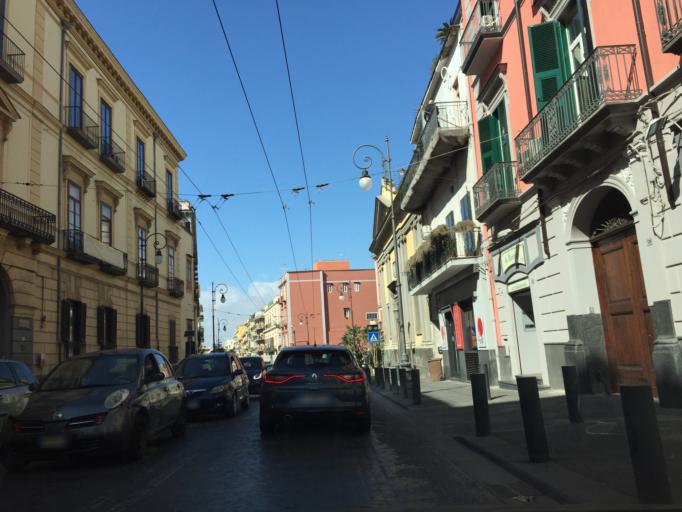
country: IT
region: Campania
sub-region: Provincia di Napoli
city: Portici
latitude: 40.8159
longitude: 14.3344
